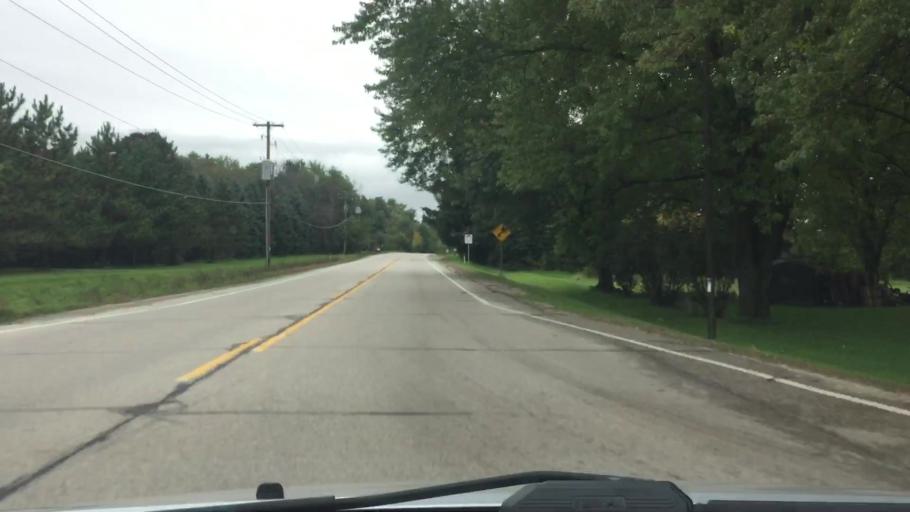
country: US
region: Wisconsin
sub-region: Walworth County
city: Elkhorn
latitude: 42.7708
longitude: -88.5552
